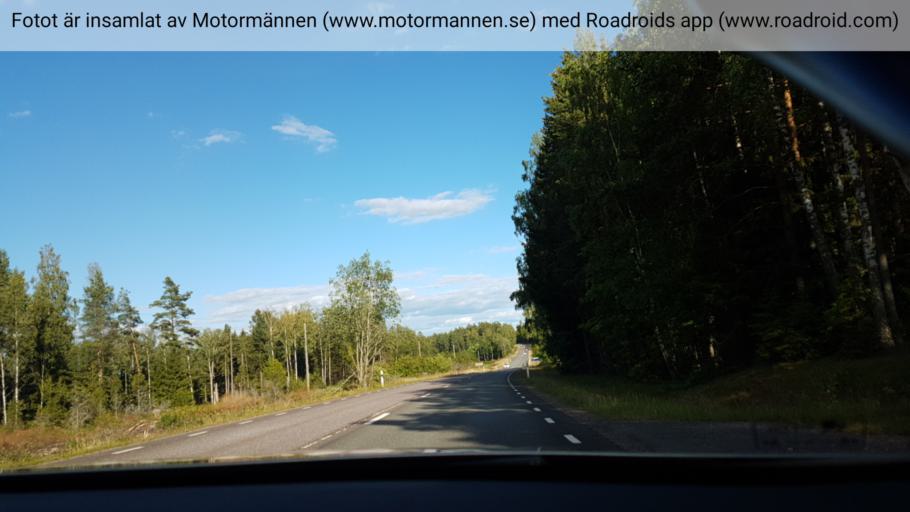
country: SE
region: Vaestra Goetaland
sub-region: Karlsborgs Kommun
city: Molltorp
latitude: 58.4908
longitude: 14.3822
